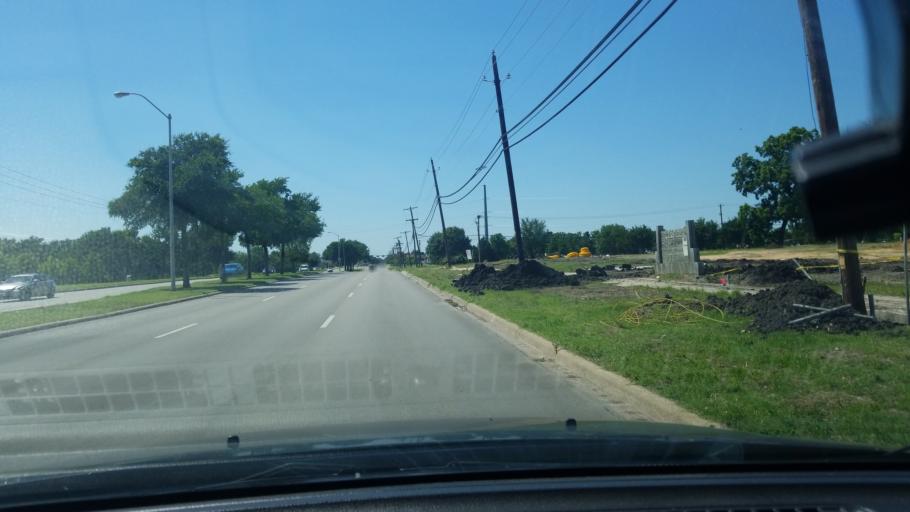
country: US
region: Texas
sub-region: Dallas County
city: Mesquite
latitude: 32.7739
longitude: -96.6155
